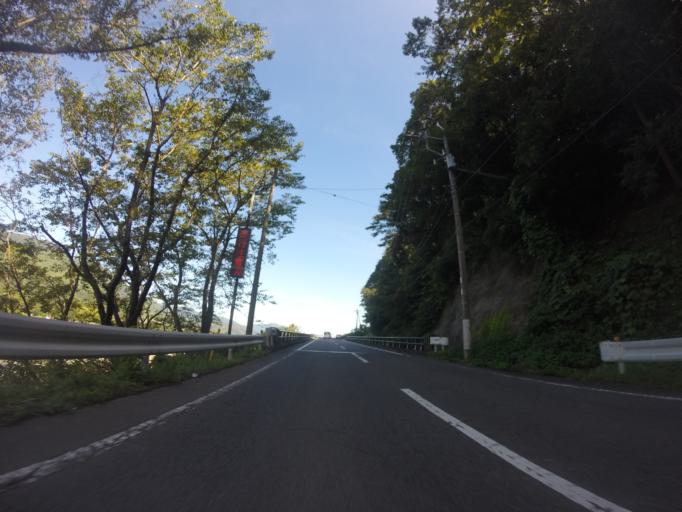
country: JP
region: Shizuoka
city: Fujinomiya
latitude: 35.2979
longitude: 138.4563
